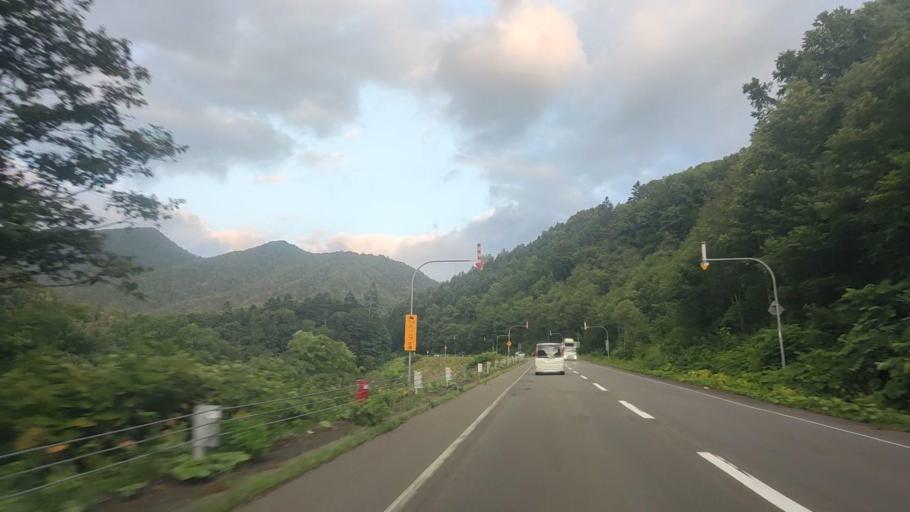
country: JP
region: Hokkaido
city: Ashibetsu
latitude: 43.3658
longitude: 142.2303
